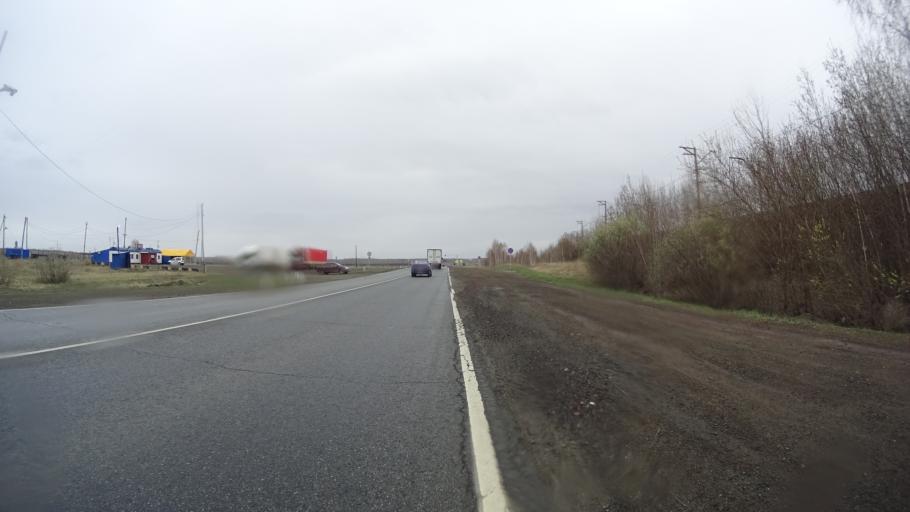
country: RU
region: Chelyabinsk
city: Krasnogorskiy
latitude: 54.6246
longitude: 61.2781
